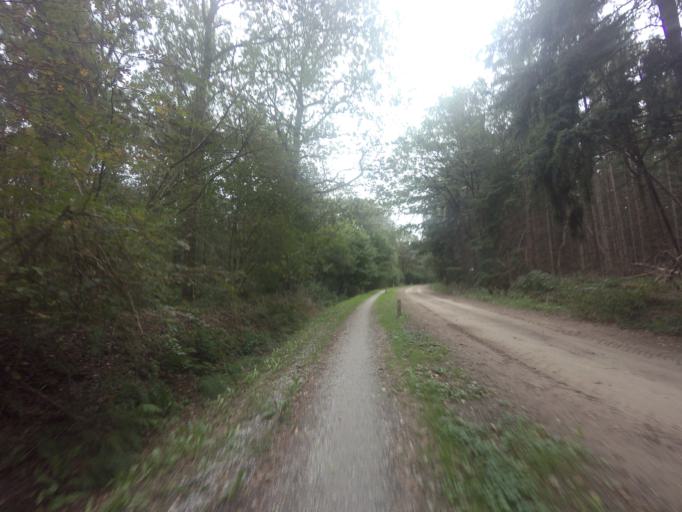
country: NL
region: Friesland
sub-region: Gemeente Weststellingwerf
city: Noordwolde
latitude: 52.9206
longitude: 6.1972
